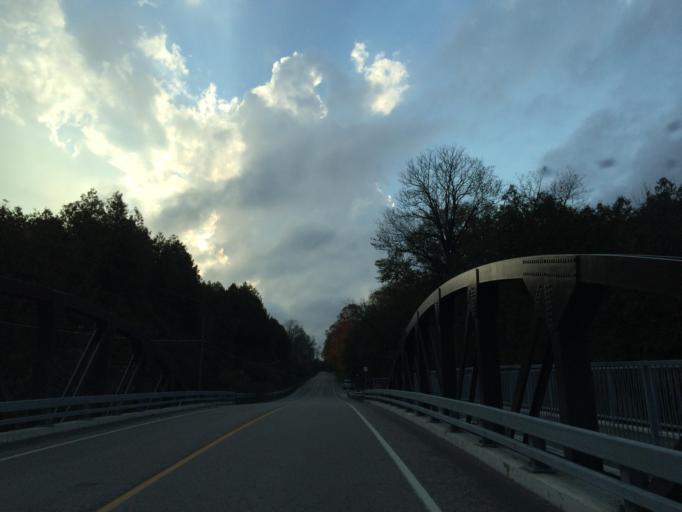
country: CA
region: Ontario
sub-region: Wellington County
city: Guelph
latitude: 43.5024
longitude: -80.2537
